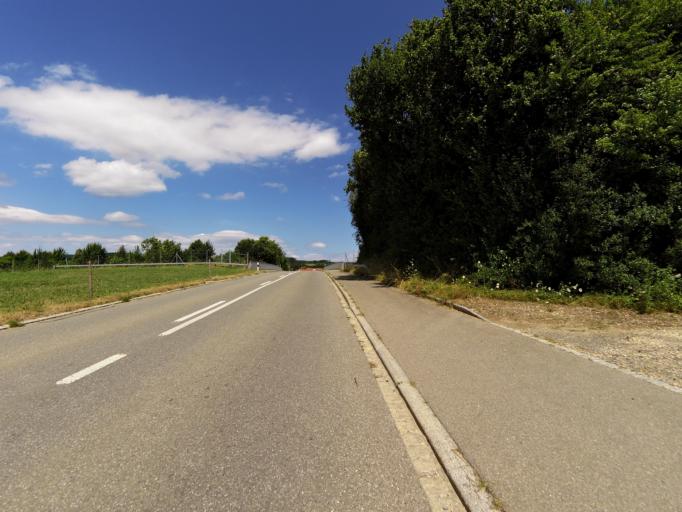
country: CH
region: Thurgau
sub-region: Weinfelden District
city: Maerstetten-Dorf
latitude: 47.6119
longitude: 9.0652
